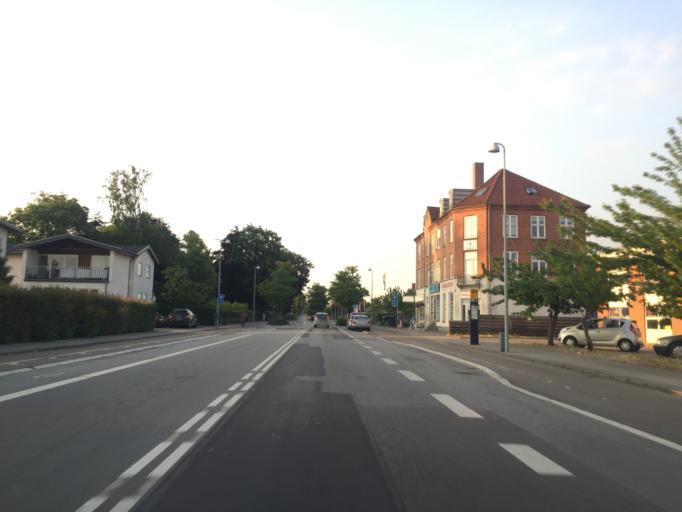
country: DK
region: Capital Region
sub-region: Hoje-Taastrup Kommune
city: Taastrup
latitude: 55.6546
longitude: 12.3058
